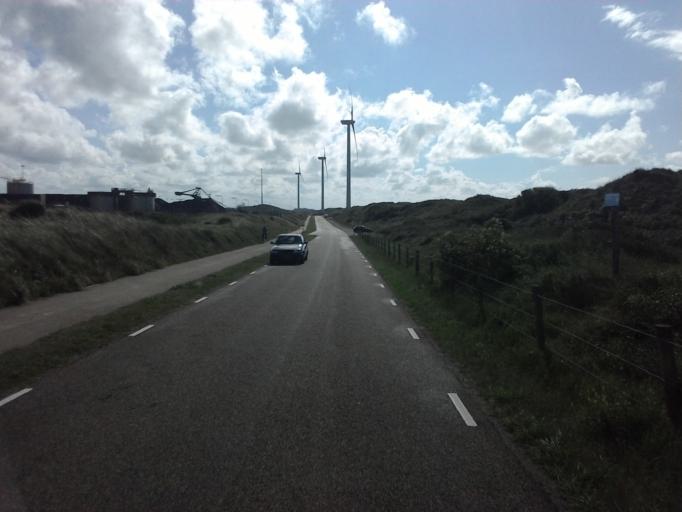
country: NL
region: North Holland
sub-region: Gemeente Velsen
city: Velsen-Zuid
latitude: 52.4797
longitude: 4.5798
